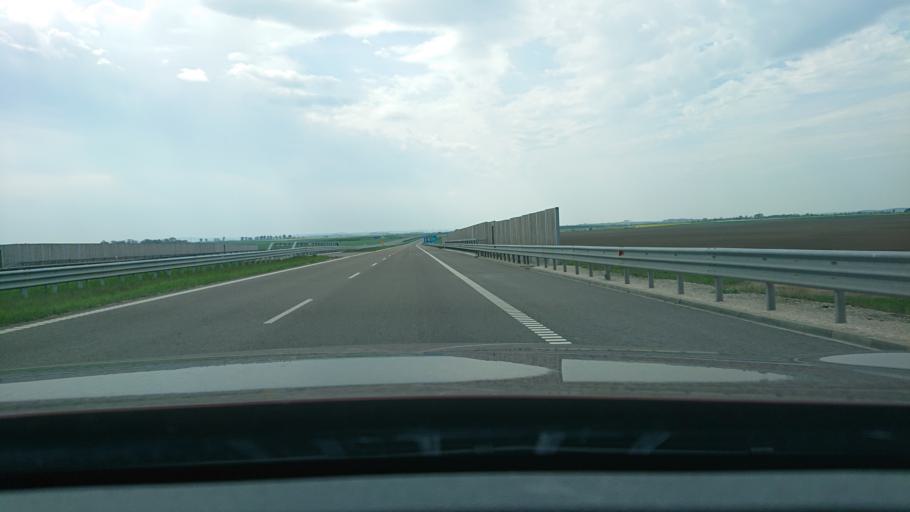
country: PL
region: Subcarpathian Voivodeship
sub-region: Powiat jaroslawski
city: Radymno
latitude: 49.9121
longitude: 22.8380
